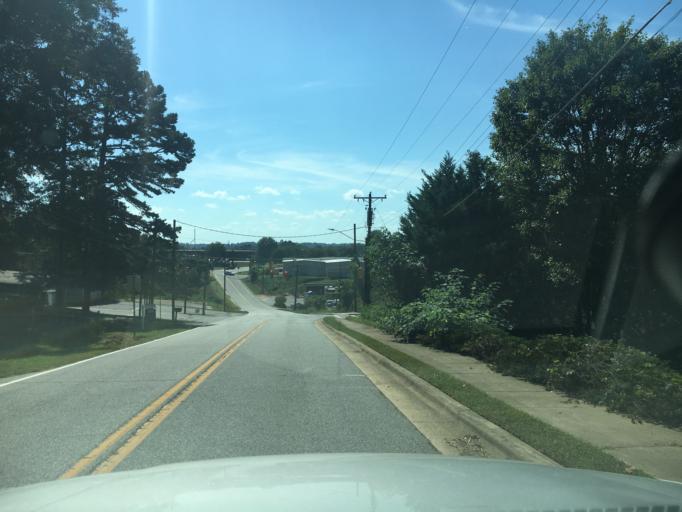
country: US
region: North Carolina
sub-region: Catawba County
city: Hickory
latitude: 35.7248
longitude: -81.3540
